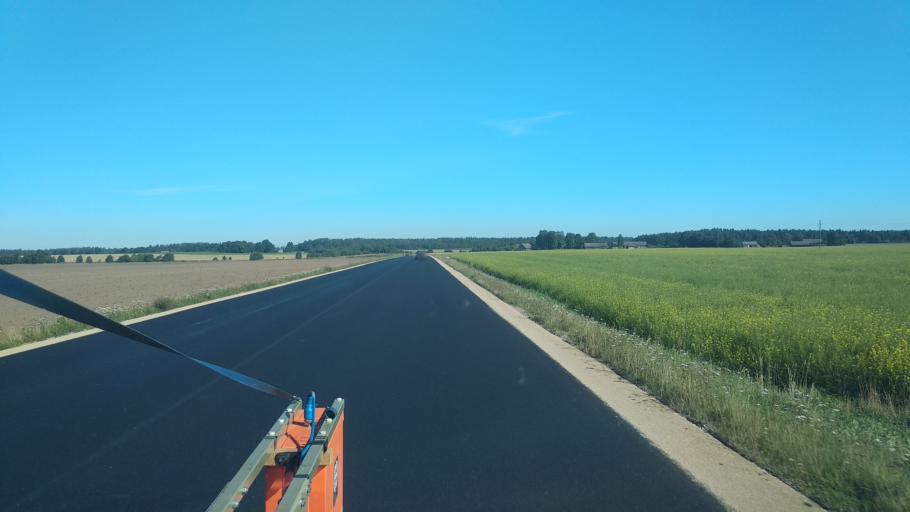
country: EE
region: Jaervamaa
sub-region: Jaerva-Jaani vald
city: Jarva-Jaani
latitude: 59.1453
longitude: 25.7714
